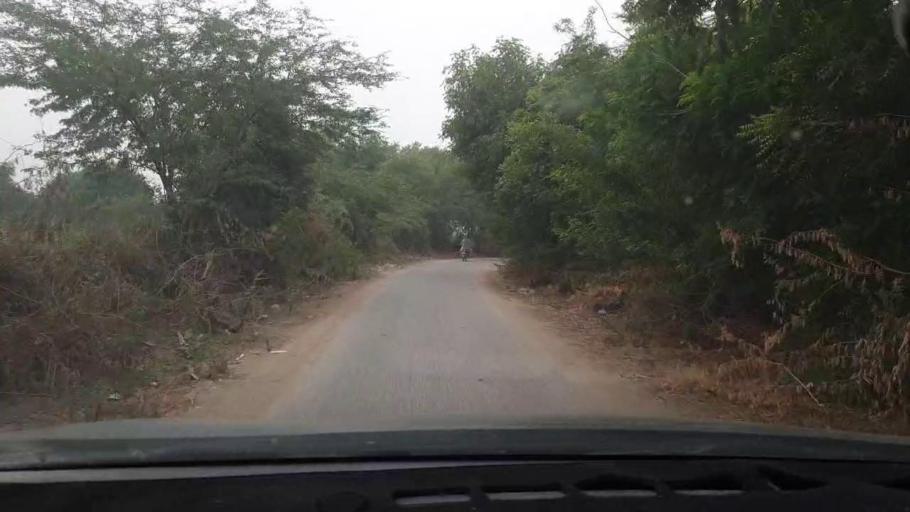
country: PK
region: Sindh
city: Malir Cantonment
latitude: 24.9252
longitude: 67.3210
